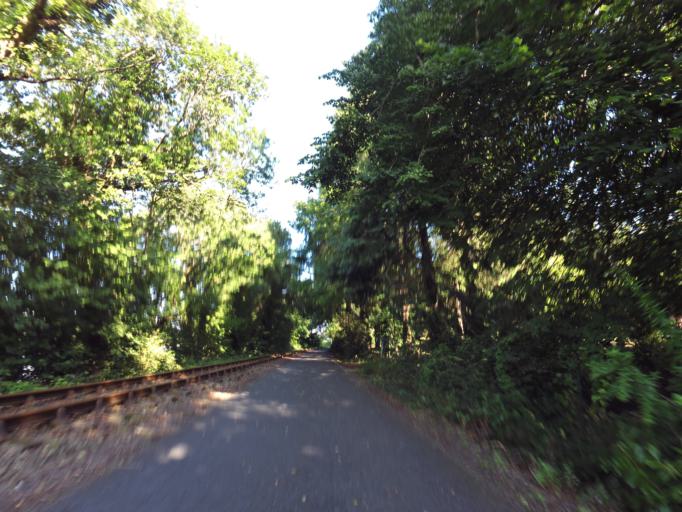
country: IE
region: Leinster
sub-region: Kilkenny
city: Mooncoin
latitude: 52.2456
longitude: -7.2283
